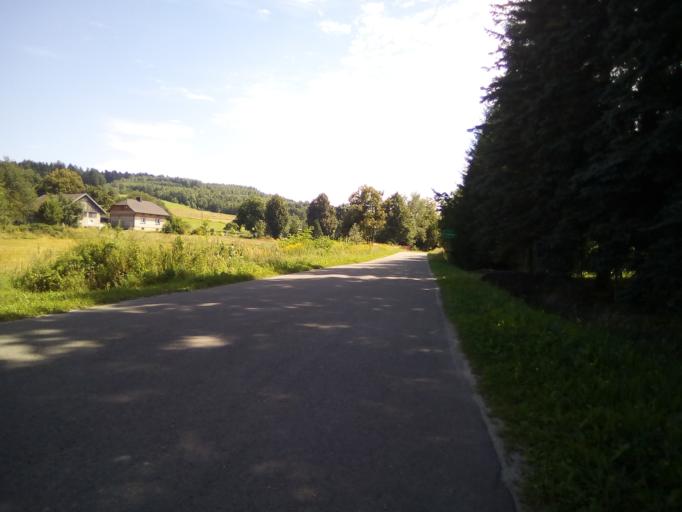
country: PL
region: Subcarpathian Voivodeship
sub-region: Powiat strzyzowski
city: Konieczkowa
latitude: 49.8239
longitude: 21.9260
